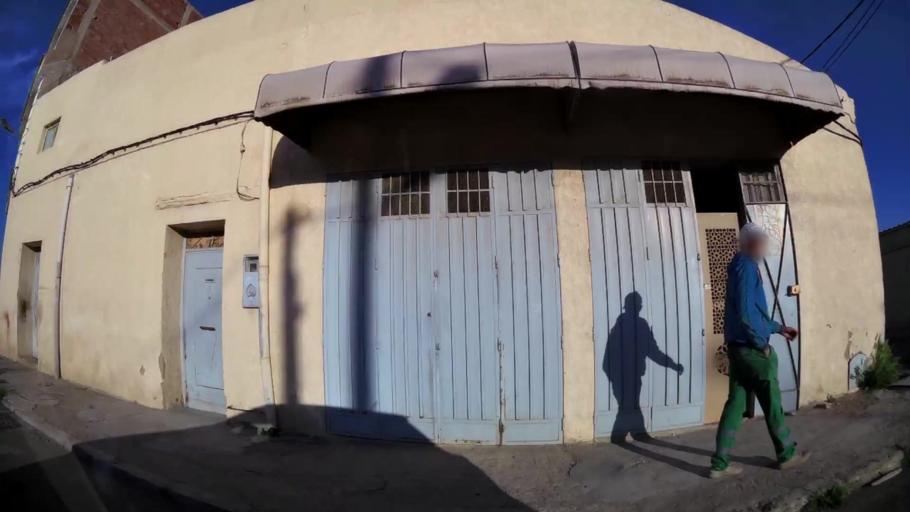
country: MA
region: Oriental
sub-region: Oujda-Angad
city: Oujda
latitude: 34.6938
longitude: -1.9077
